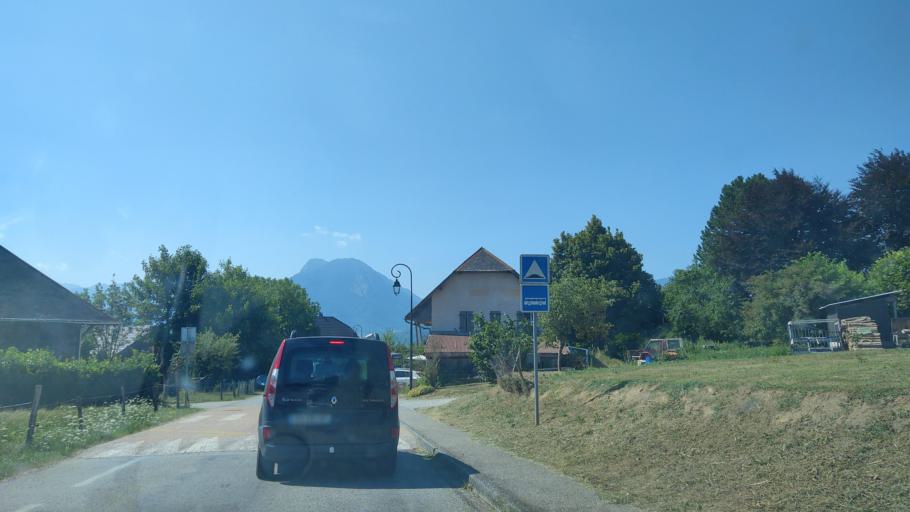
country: FR
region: Rhone-Alpes
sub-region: Departement de la Haute-Savoie
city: Gruffy
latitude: 45.7444
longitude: 6.1144
